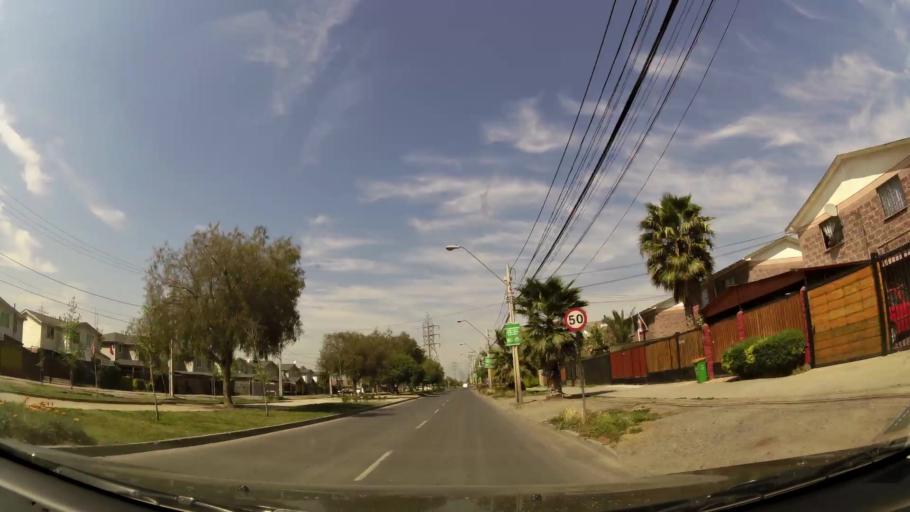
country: CL
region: Santiago Metropolitan
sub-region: Provincia de Santiago
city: La Pintana
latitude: -33.5744
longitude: -70.5992
